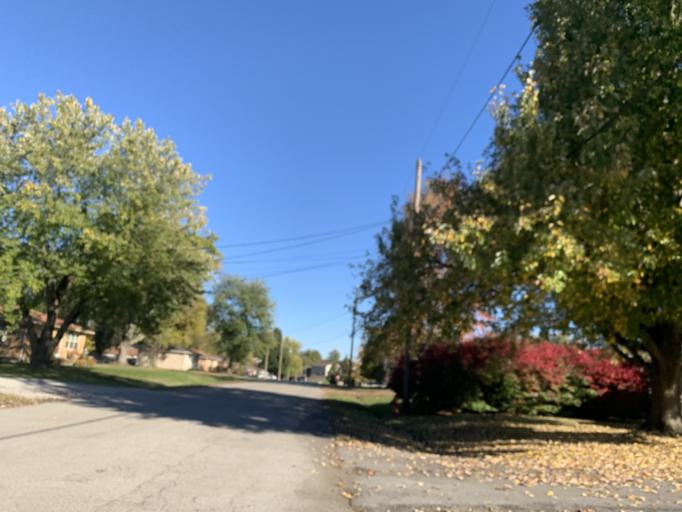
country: US
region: Kentucky
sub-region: Jefferson County
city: Pleasure Ridge Park
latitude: 38.1599
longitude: -85.8655
